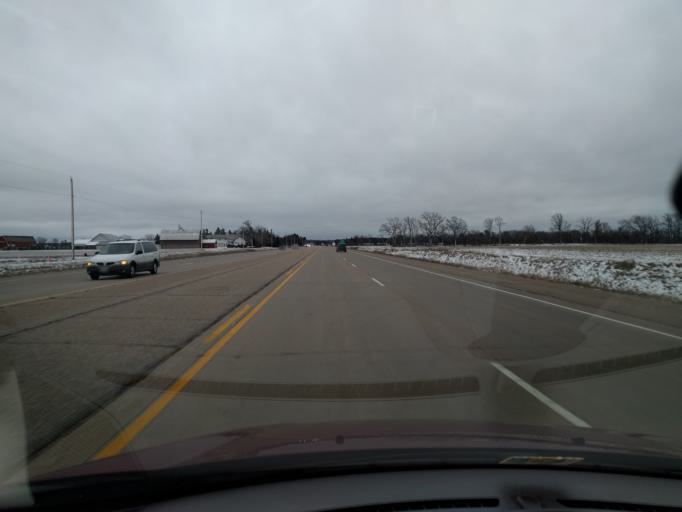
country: US
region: Wisconsin
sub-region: Portage County
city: Whiting
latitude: 44.5229
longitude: -89.4801
